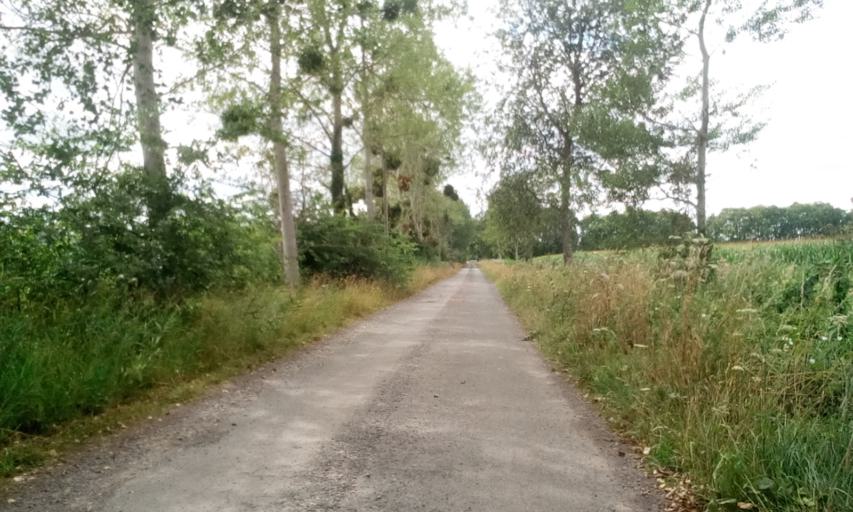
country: FR
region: Lower Normandy
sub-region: Departement du Calvados
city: Bellengreville
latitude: 49.1431
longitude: -0.2012
